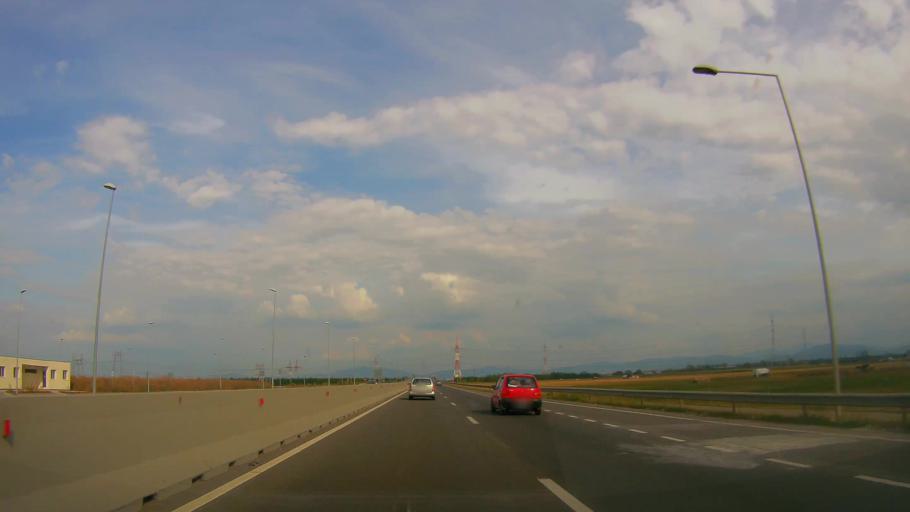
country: RO
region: Brasov
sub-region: Comuna Sanpetru
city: Sanpetru
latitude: 45.6885
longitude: 25.6397
